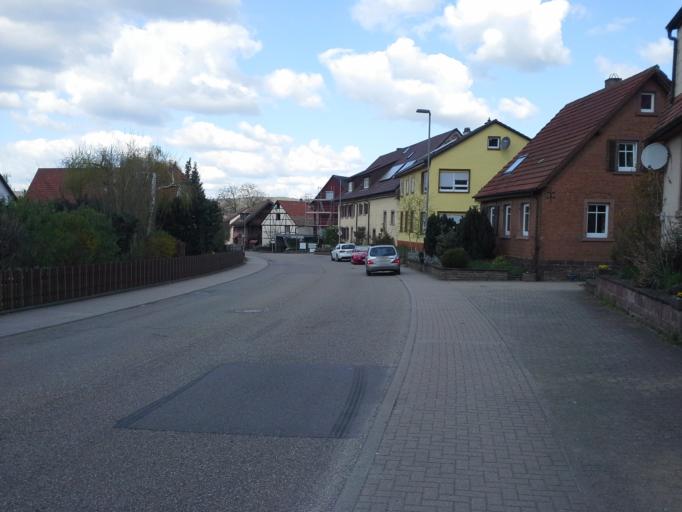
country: DE
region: Baden-Wuerttemberg
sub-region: Karlsruhe Region
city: Neuenburg
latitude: 48.9004
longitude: 8.5806
